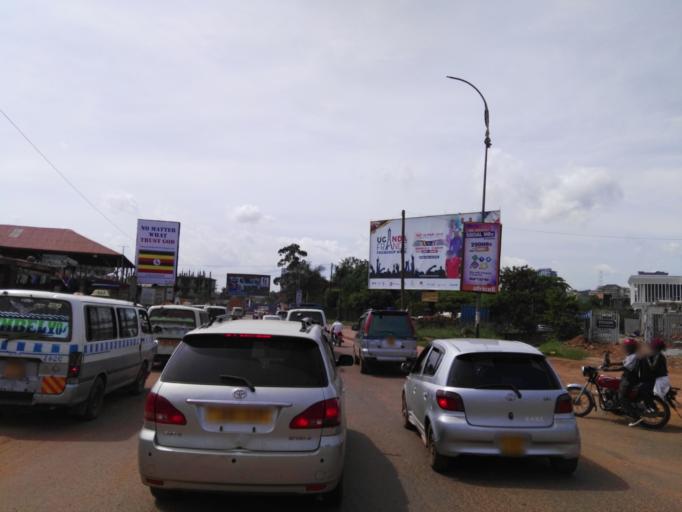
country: UG
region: Central Region
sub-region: Kampala District
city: Kampala
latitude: 0.3050
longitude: 32.5771
